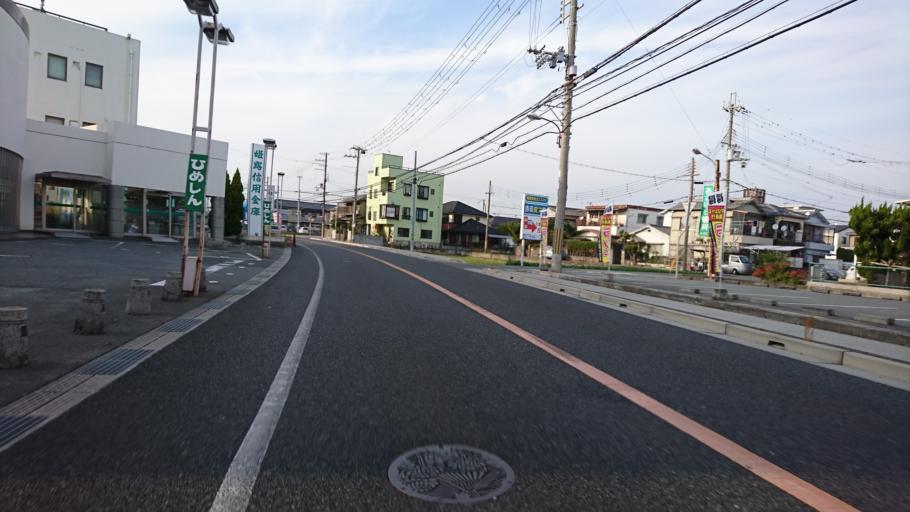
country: JP
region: Hyogo
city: Kakogawacho-honmachi
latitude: 34.7165
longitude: 134.8604
